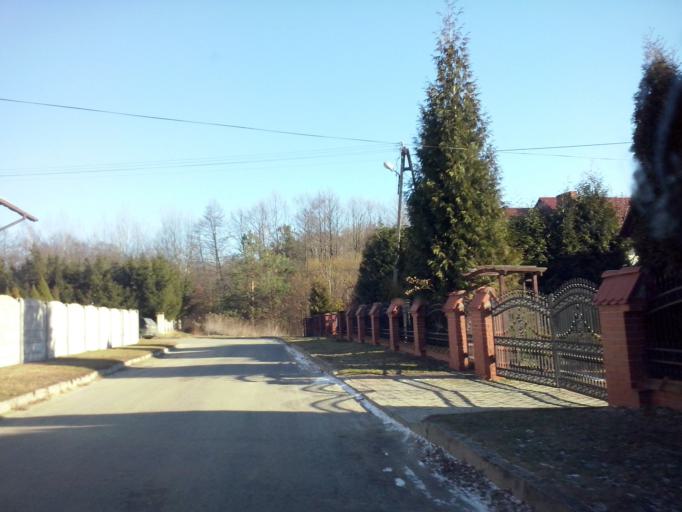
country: PL
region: Subcarpathian Voivodeship
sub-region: Powiat nizanski
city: Krzeszow
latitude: 50.4114
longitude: 22.3432
